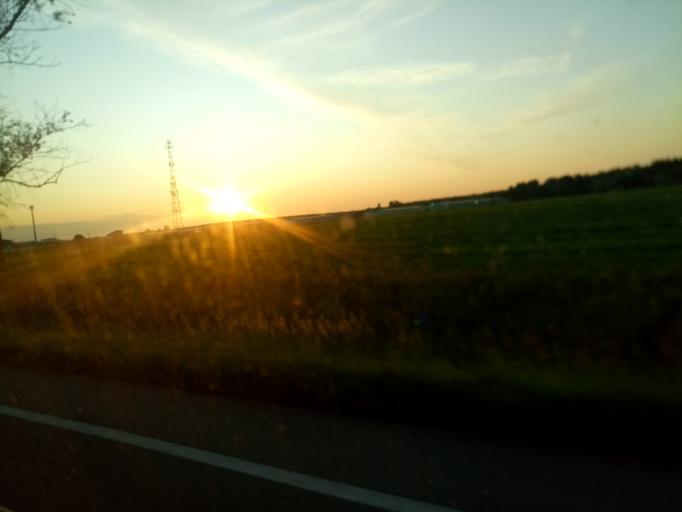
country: RU
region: Moskovskaya
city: Noginsk-9
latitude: 56.0460
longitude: 38.4947
